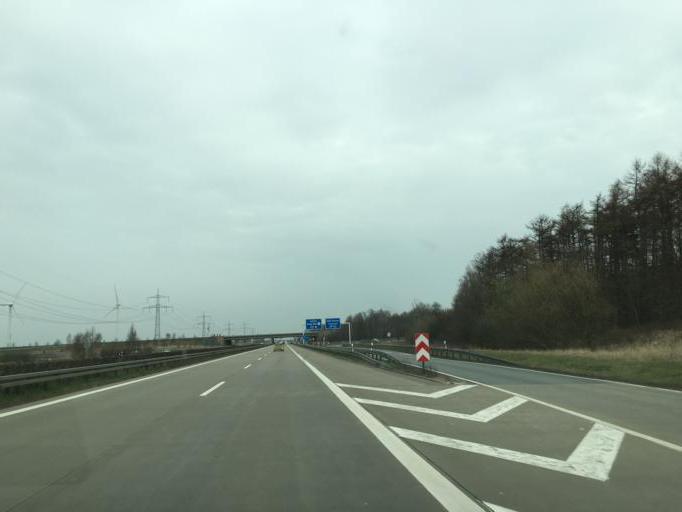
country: DE
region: Mecklenburg-Vorpommern
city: Kavelstorf
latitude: 54.0241
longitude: 12.2011
